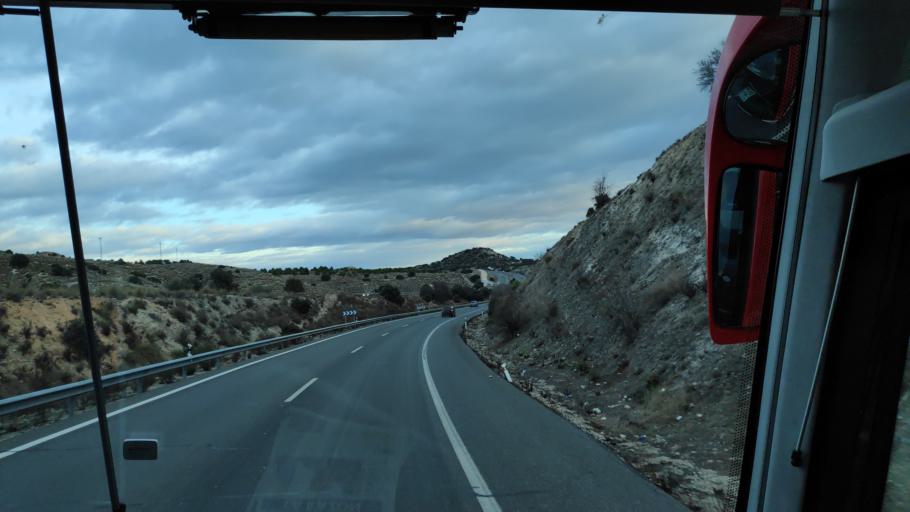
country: ES
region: Madrid
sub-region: Provincia de Madrid
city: Villarejo de Salvanes
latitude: 40.1480
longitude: -3.2198
